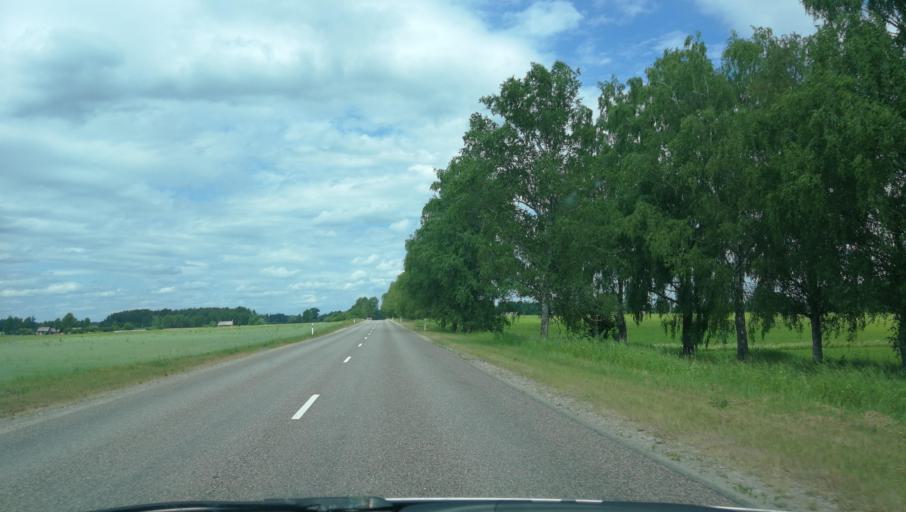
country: LV
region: Rujienas
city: Rujiena
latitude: 57.8357
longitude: 25.3876
